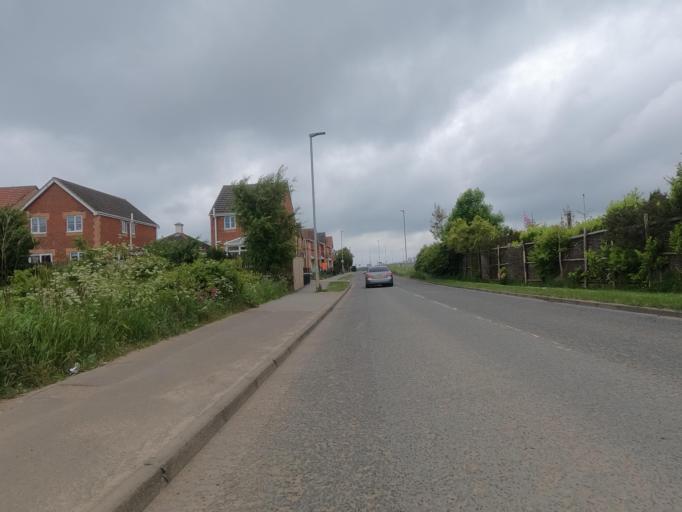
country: GB
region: England
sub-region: Northumberland
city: Blyth
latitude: 55.1050
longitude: -1.5279
